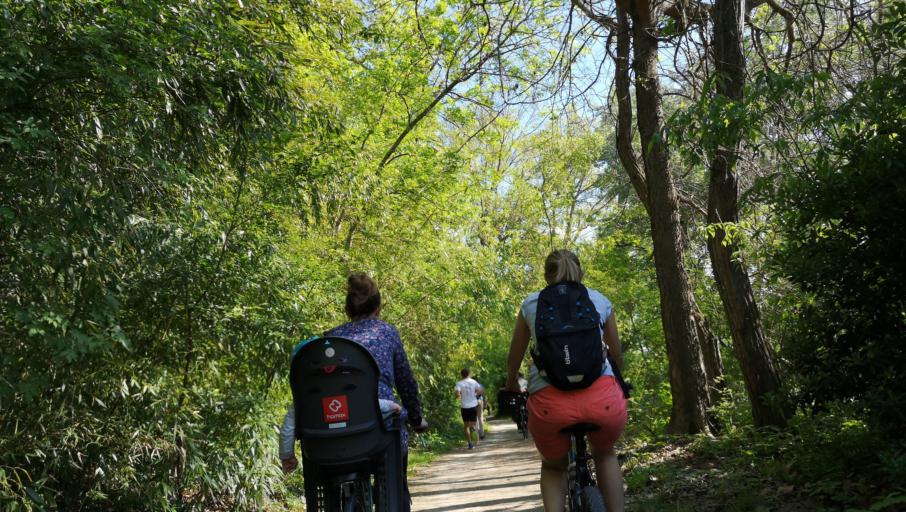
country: FR
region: Midi-Pyrenees
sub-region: Departement de la Haute-Garonne
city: Blagnac
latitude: 43.6398
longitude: 1.4044
